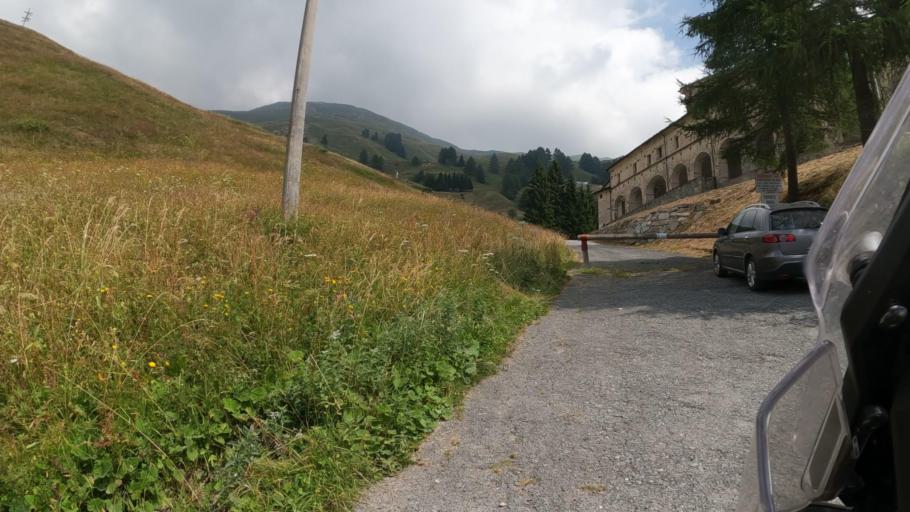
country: IT
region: Piedmont
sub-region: Provincia di Cuneo
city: Campomolino
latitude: 44.4003
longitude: 7.1704
